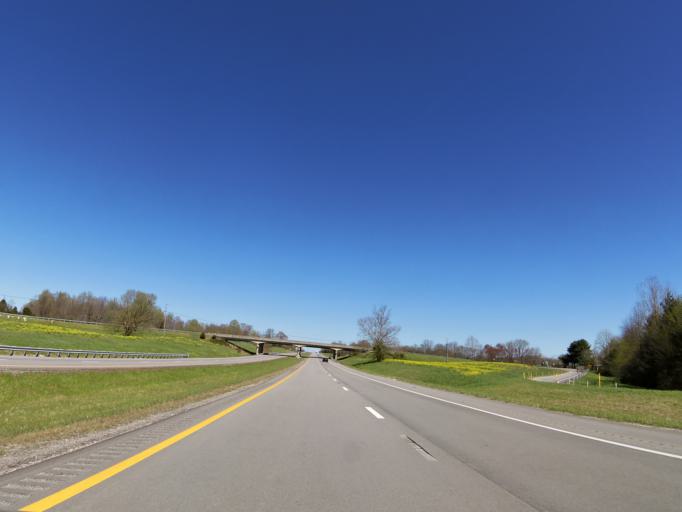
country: US
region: Kentucky
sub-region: Pulaski County
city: Somerset
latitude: 37.0920
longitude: -84.8039
